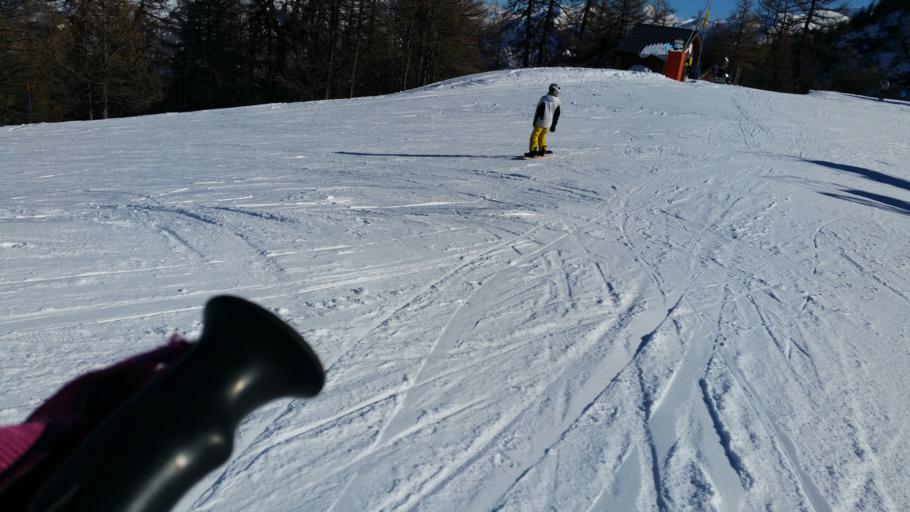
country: FR
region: Rhone-Alpes
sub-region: Departement de la Savoie
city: Villargondran
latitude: 45.2188
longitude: 6.3971
